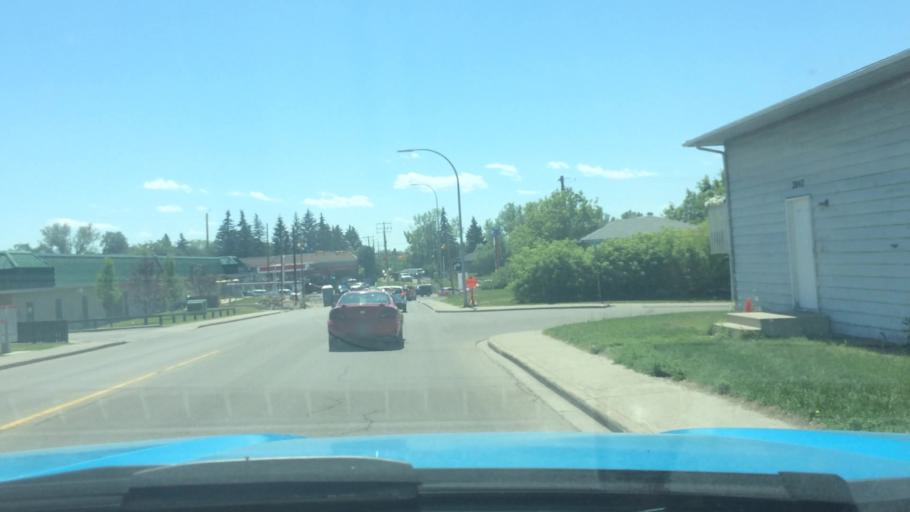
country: CA
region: Alberta
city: Calgary
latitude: 51.0390
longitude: -113.9932
